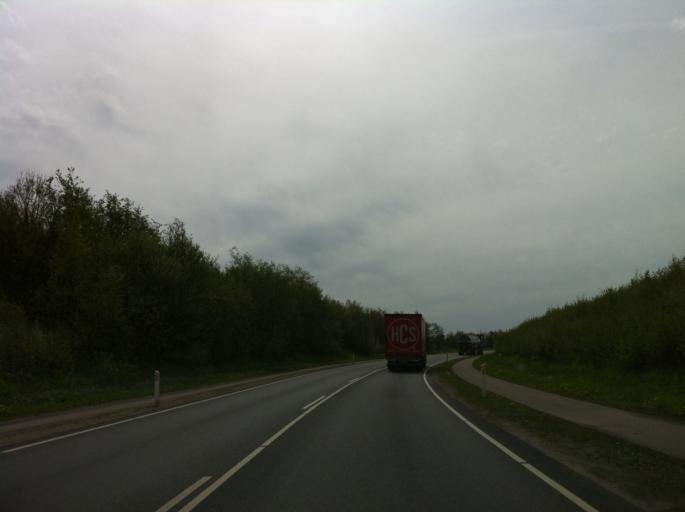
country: DK
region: Zealand
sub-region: Ringsted Kommune
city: Ringsted
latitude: 55.4412
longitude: 11.8255
